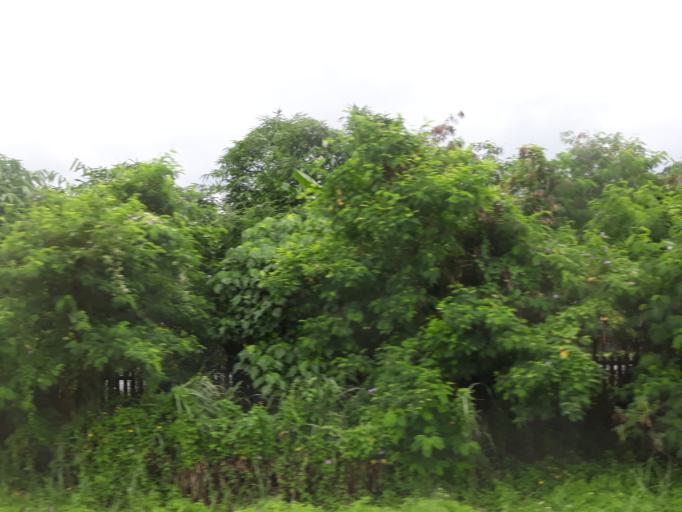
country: TW
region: Taiwan
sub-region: Yilan
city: Yilan
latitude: 24.6154
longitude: 121.8134
